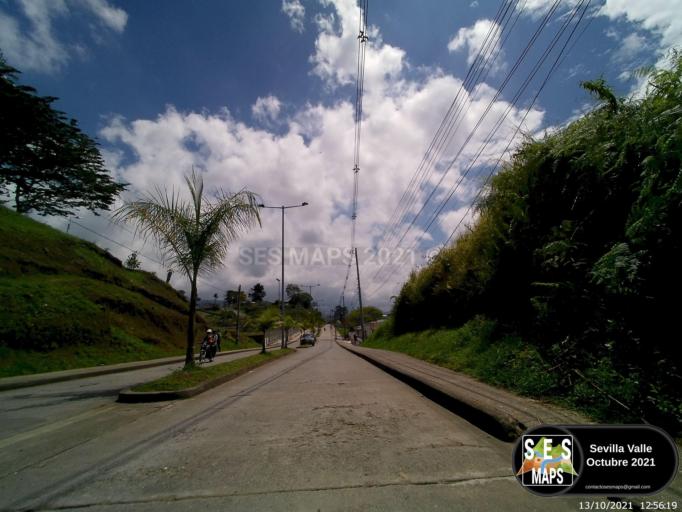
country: CO
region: Valle del Cauca
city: Sevilla
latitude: 4.2720
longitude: -75.9319
